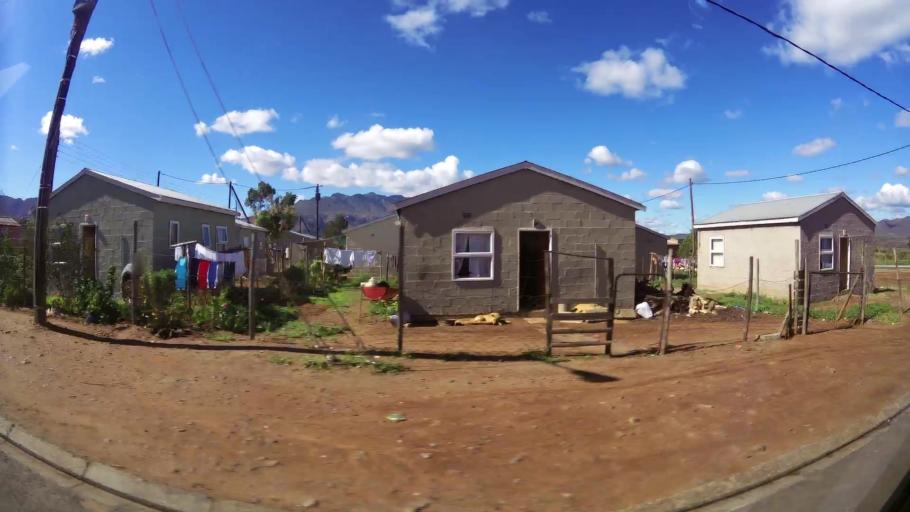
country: ZA
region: Western Cape
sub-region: Cape Winelands District Municipality
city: Ashton
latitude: -33.8354
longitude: 20.0434
